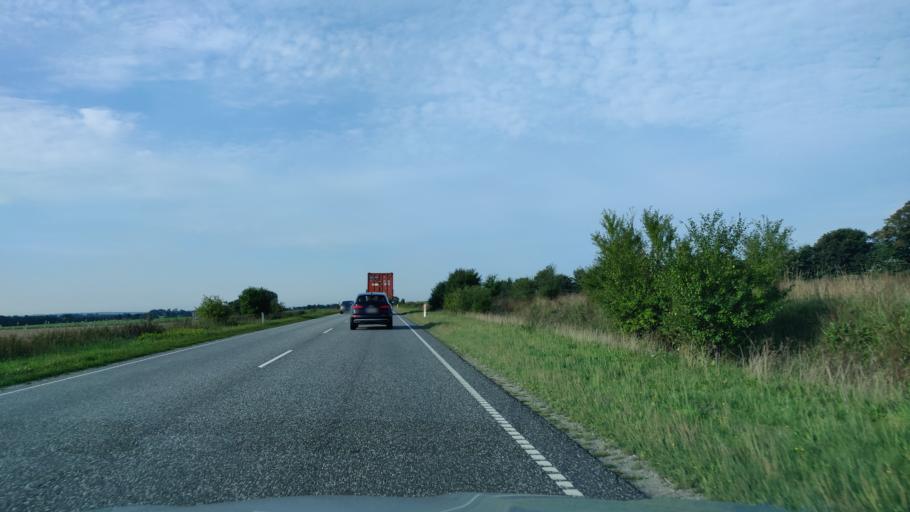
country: DK
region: North Denmark
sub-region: Vesthimmerland Kommune
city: Aars
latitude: 56.7849
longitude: 9.5931
